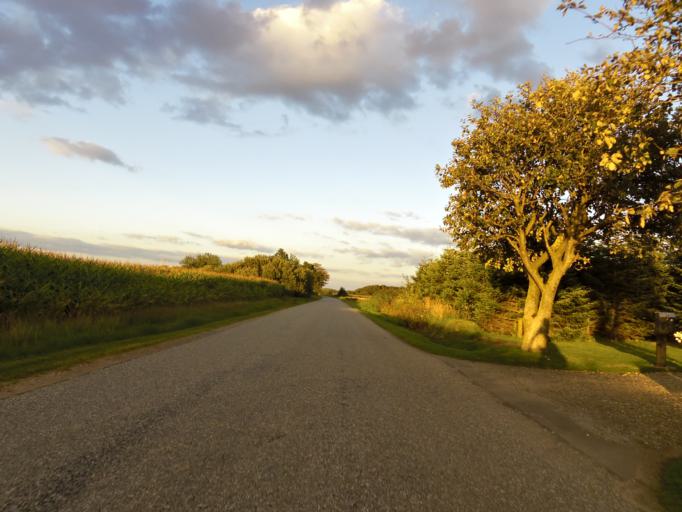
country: DK
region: South Denmark
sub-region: Tonder Kommune
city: Sherrebek
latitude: 55.2414
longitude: 8.8836
